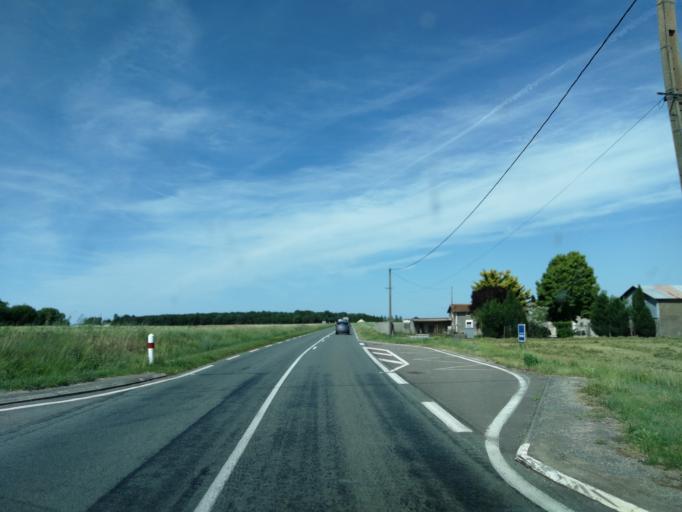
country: FR
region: Poitou-Charentes
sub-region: Departement de la Vienne
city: Loudun
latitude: 47.0353
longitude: 0.1226
